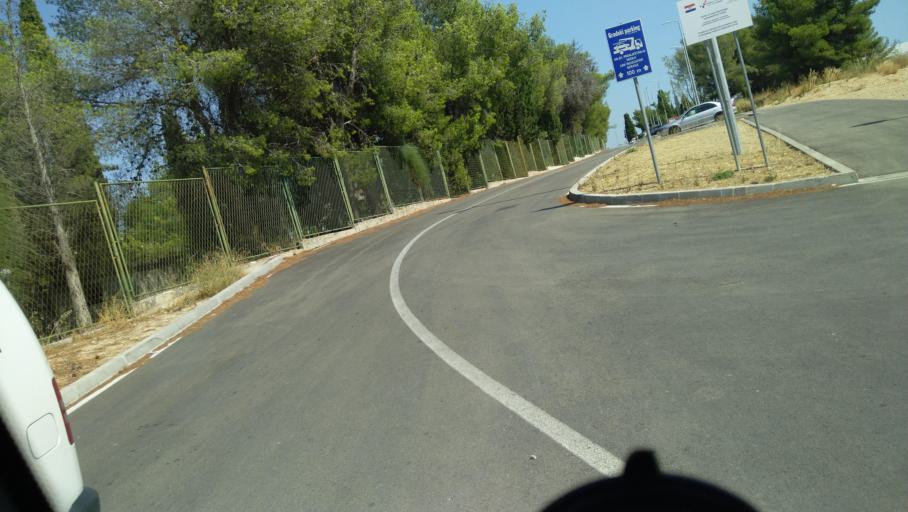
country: HR
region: Sibensko-Kniniska
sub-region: Grad Sibenik
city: Sibenik
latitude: 43.7176
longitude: 15.9066
